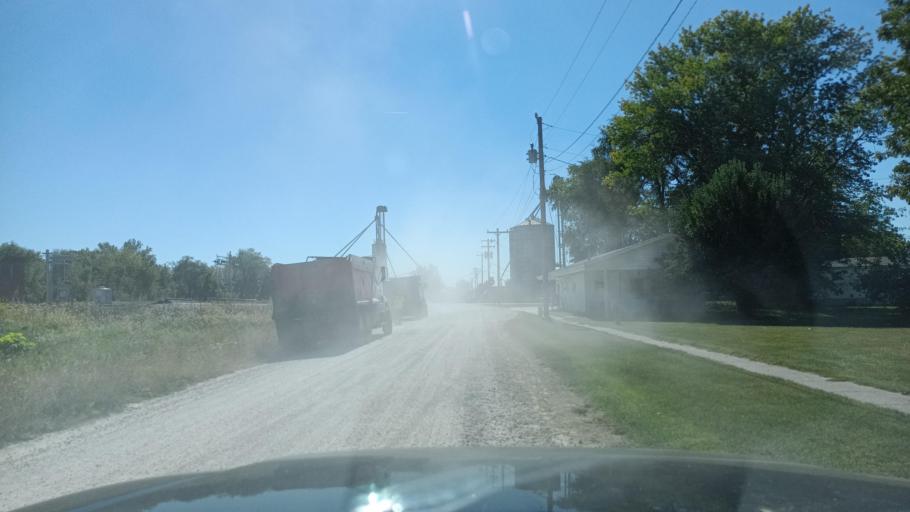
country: US
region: Missouri
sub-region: Macon County
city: La Plata
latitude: 39.9579
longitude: -92.6502
